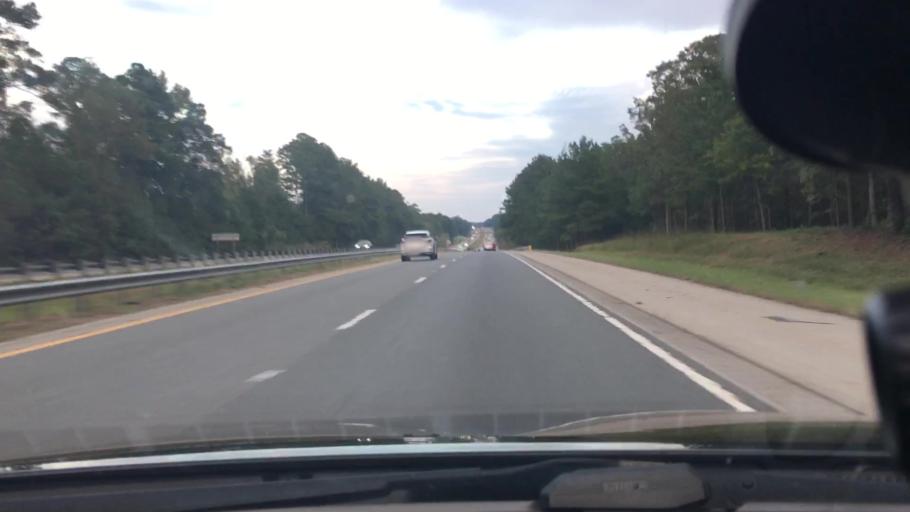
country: US
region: North Carolina
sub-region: Chatham County
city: Pittsboro
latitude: 35.6305
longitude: -79.0671
